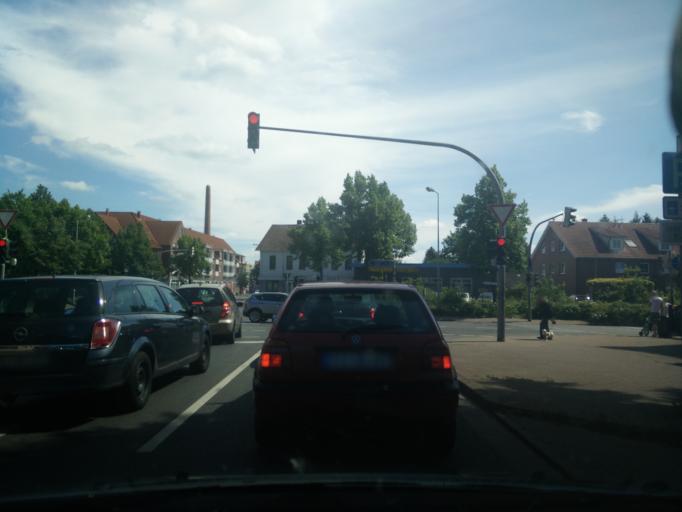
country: DE
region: Schleswig-Holstein
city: Tornesch
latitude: 53.6975
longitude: 9.7119
